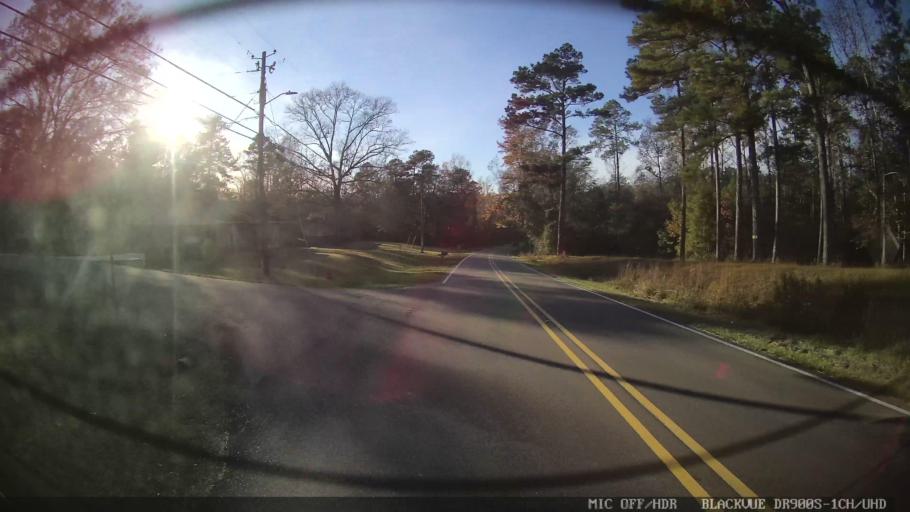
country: US
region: Mississippi
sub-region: Lamar County
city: Purvis
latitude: 31.1456
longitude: -89.4195
